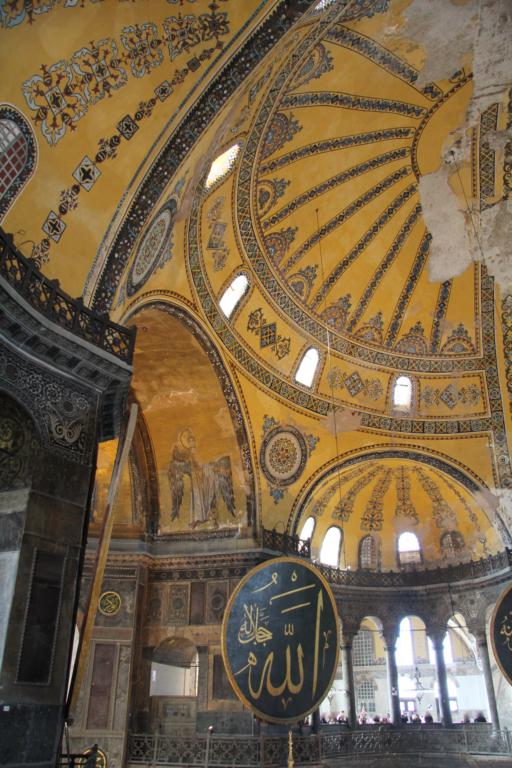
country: TR
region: Istanbul
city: Eminoenue
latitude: 41.0086
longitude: 28.9800
